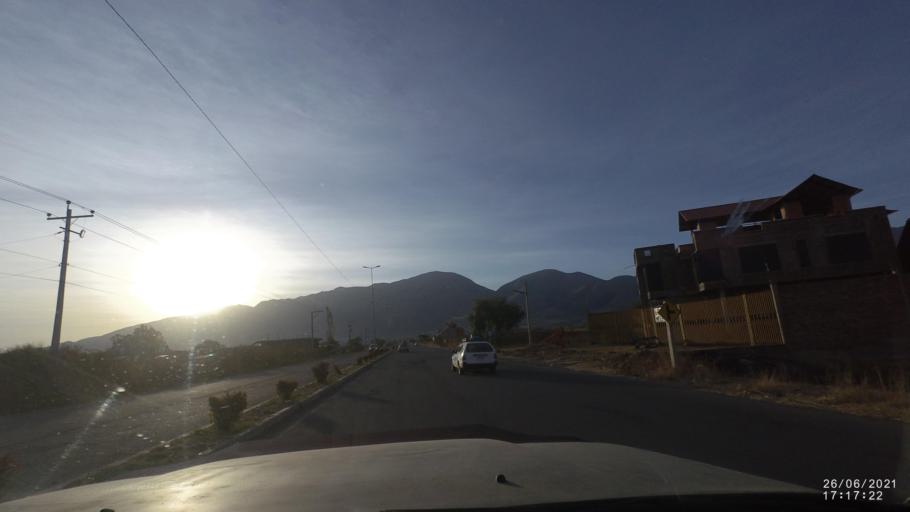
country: BO
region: Cochabamba
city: Cliza
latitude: -17.5492
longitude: -65.9500
